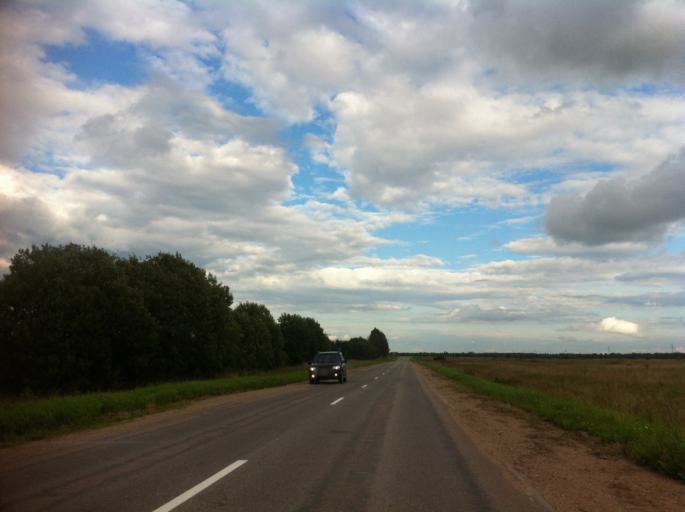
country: RU
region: Pskov
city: Izborsk
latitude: 57.8365
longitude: 28.0446
